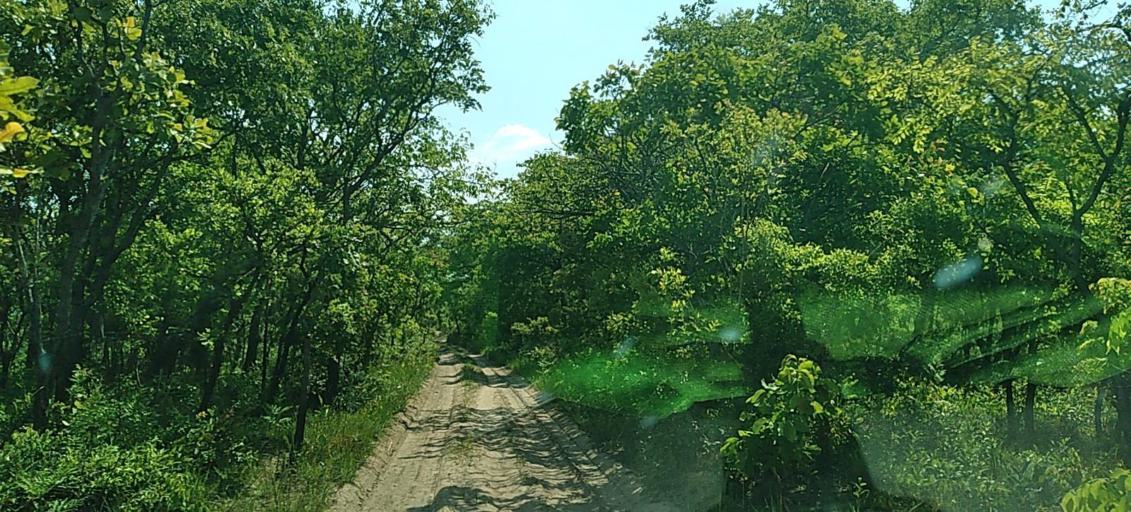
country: CD
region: Katanga
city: Kolwezi
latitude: -11.2616
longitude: 25.0066
